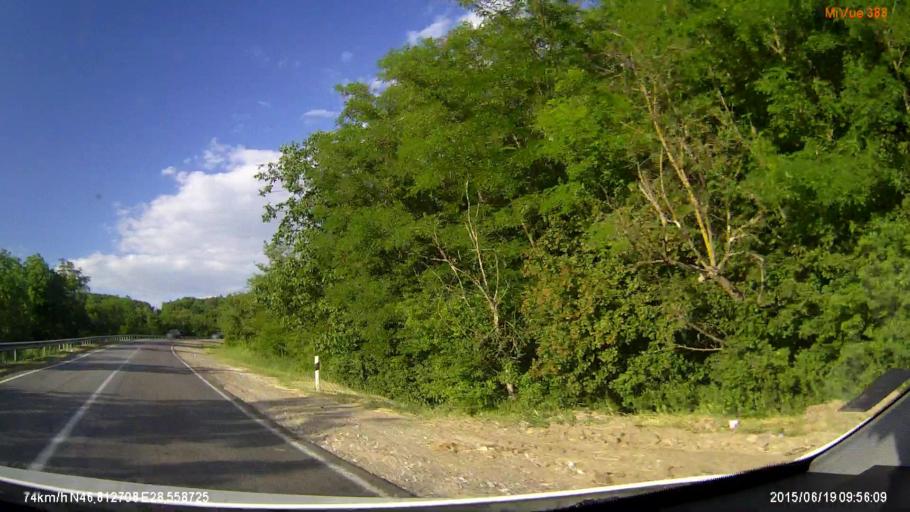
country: MD
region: Hincesti
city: Hincesti
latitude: 46.8124
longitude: 28.5584
